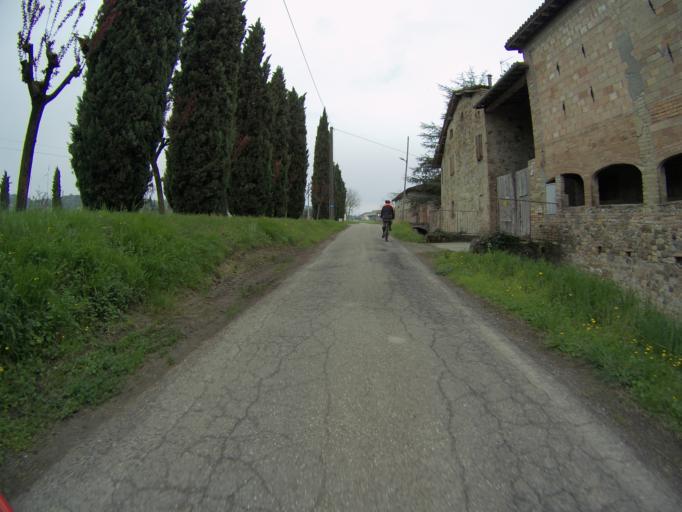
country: IT
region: Emilia-Romagna
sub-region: Provincia di Reggio Emilia
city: San Polo d'Enza
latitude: 44.6396
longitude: 10.4416
